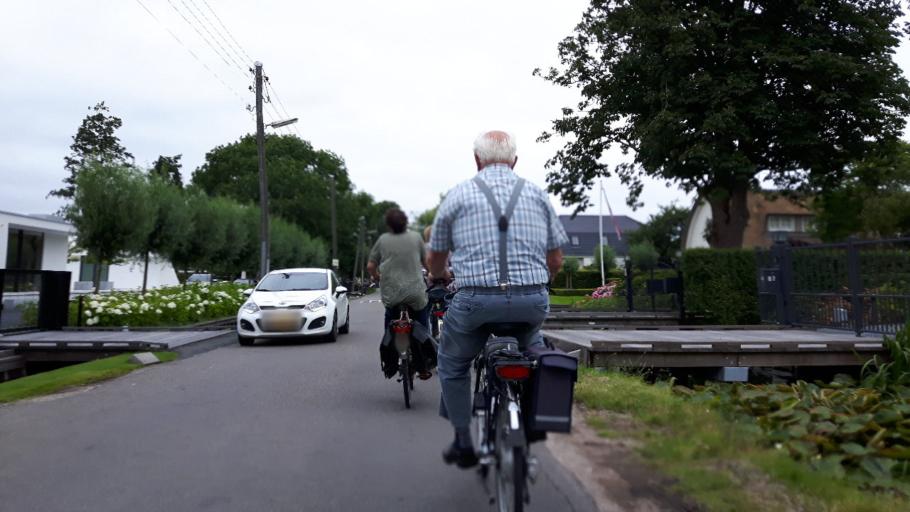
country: NL
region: South Holland
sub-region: Bodegraven-Reeuwijk
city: Reeuwijk
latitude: 52.0398
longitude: 4.7393
